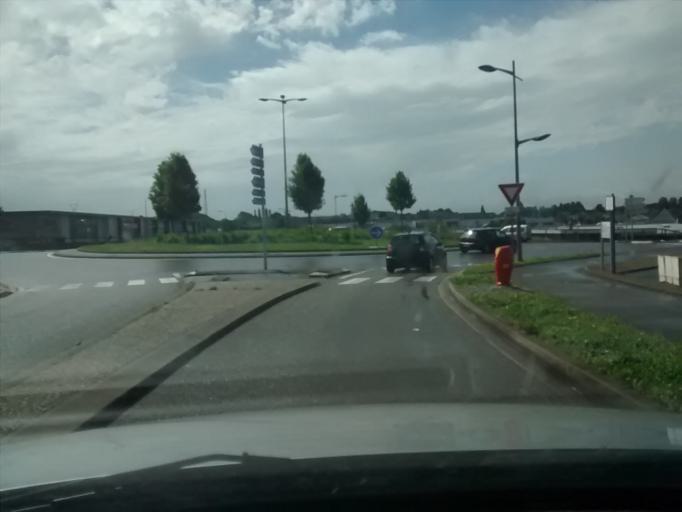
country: FR
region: Pays de la Loire
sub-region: Departement de la Mayenne
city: Saint-Berthevin
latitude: 48.0692
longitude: -0.8081
